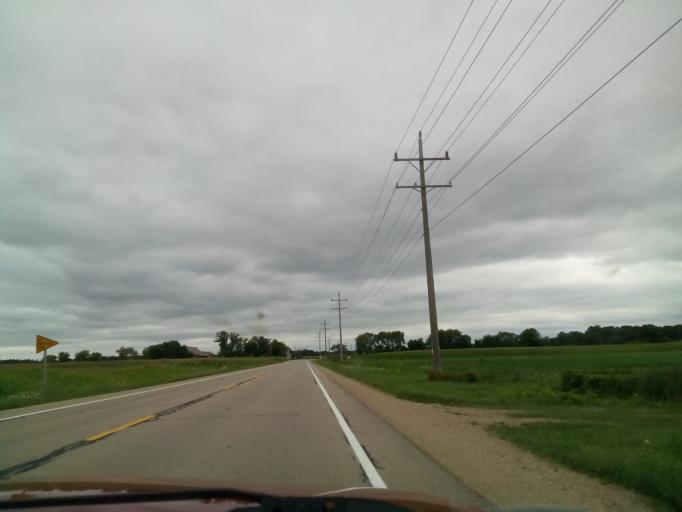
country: US
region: Wisconsin
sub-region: Waupaca County
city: New London
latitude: 44.2665
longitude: -88.7913
